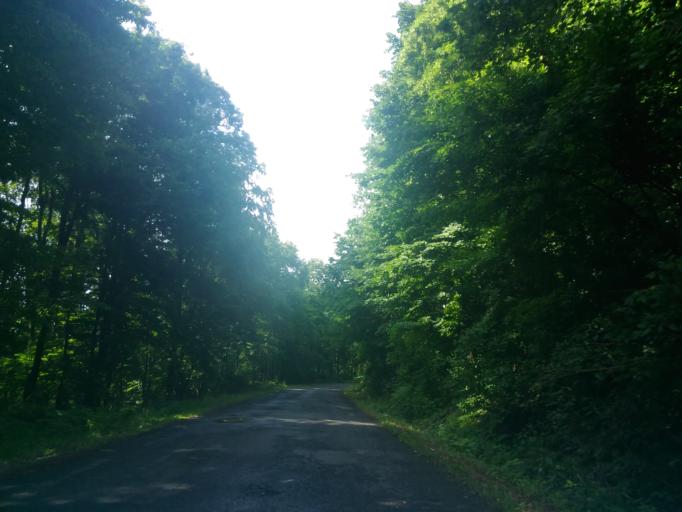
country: HU
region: Baranya
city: Pecs
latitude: 46.1348
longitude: 18.2455
